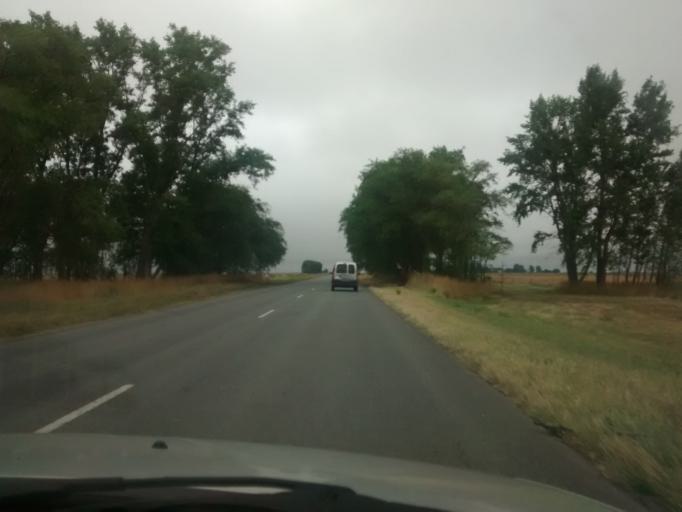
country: AR
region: Buenos Aires
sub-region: Partido de Ayacucho
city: Ayacucho
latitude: -37.2497
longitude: -58.4868
